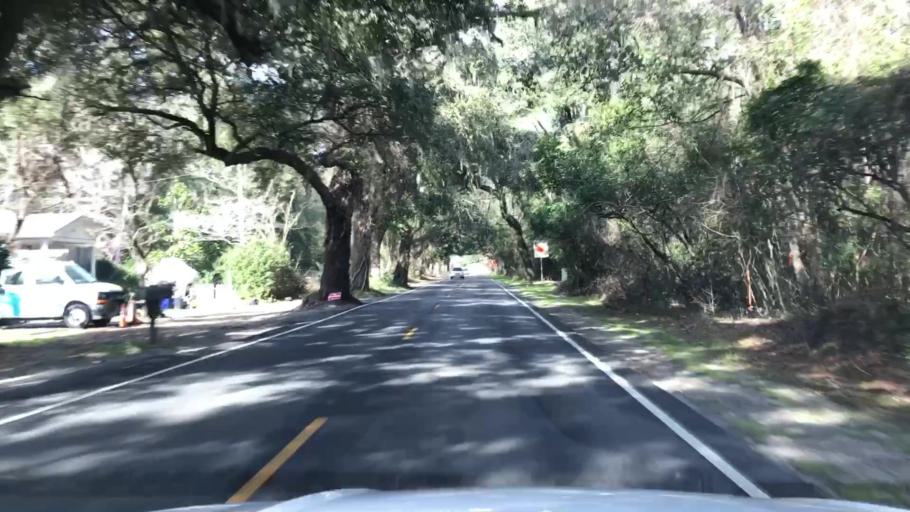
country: US
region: South Carolina
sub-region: Charleston County
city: Shell Point
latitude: 32.7384
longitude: -80.0344
